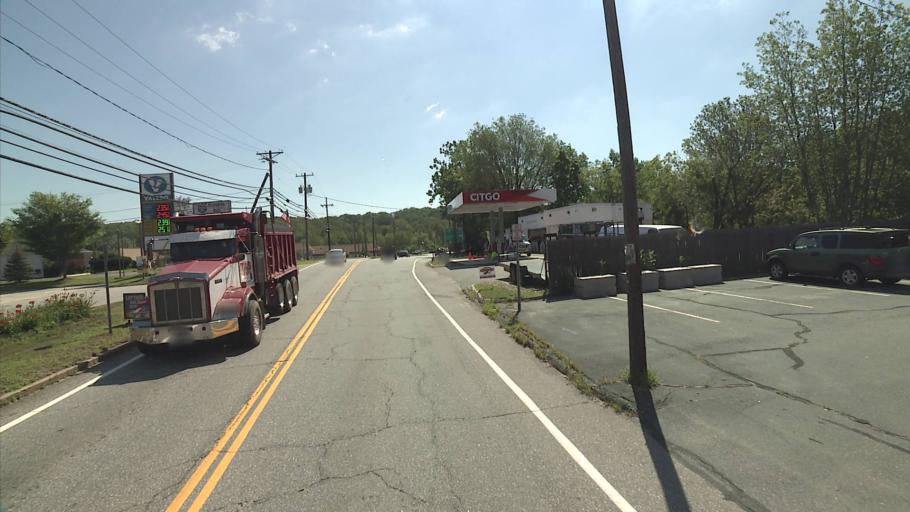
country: US
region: Connecticut
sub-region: Windham County
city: Moosup
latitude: 41.7194
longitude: -71.8983
